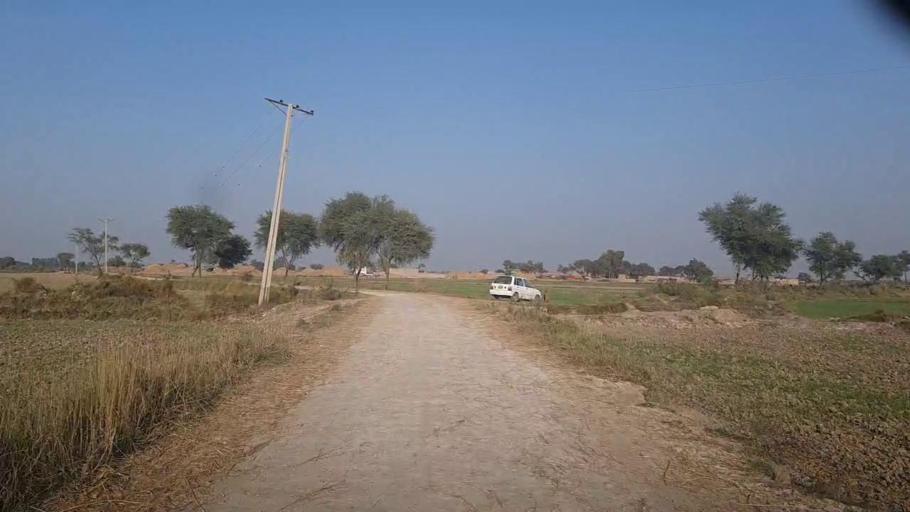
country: PK
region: Sindh
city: Thul
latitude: 28.1634
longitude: 68.8149
